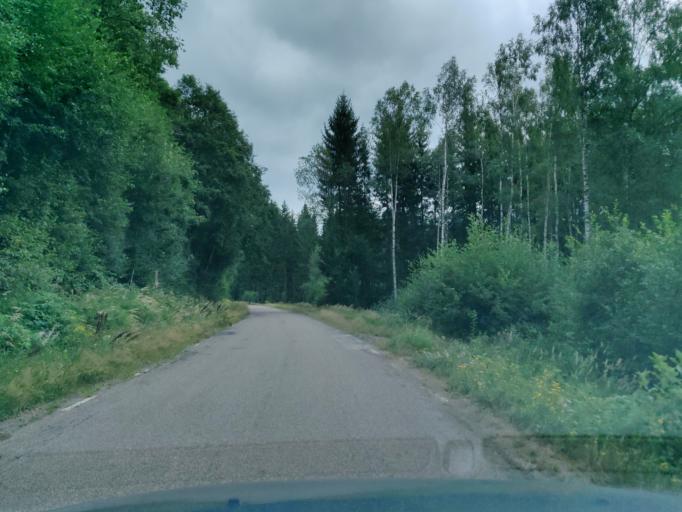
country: SE
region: Vaermland
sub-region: Munkfors Kommun
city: Munkfors
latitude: 59.9154
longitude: 13.5648
